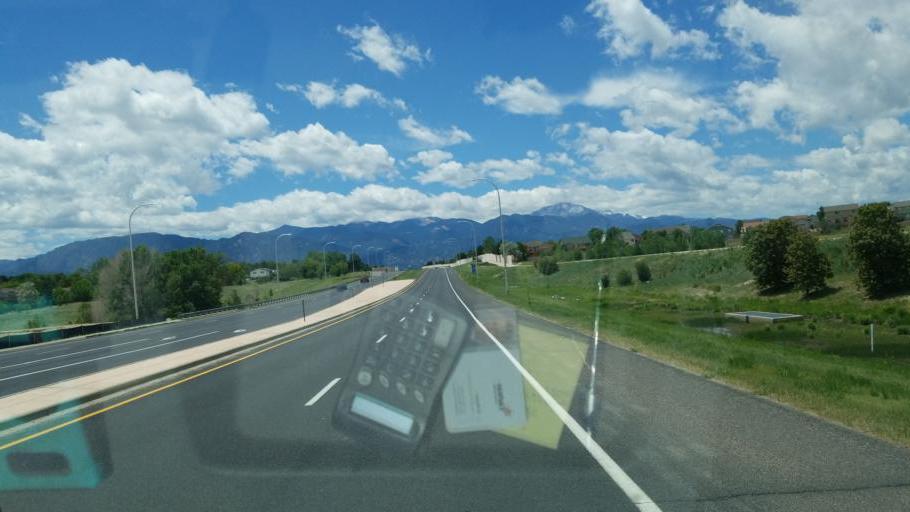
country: US
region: Colorado
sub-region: El Paso County
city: Security-Widefield
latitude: 38.7814
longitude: -104.7233
